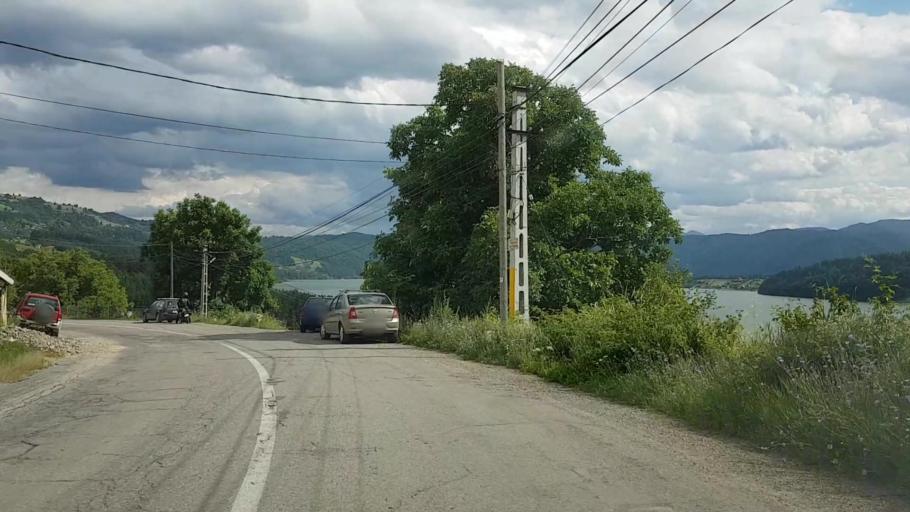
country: RO
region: Neamt
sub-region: Comuna Hangu
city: Hangu
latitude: 47.0184
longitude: 26.0731
